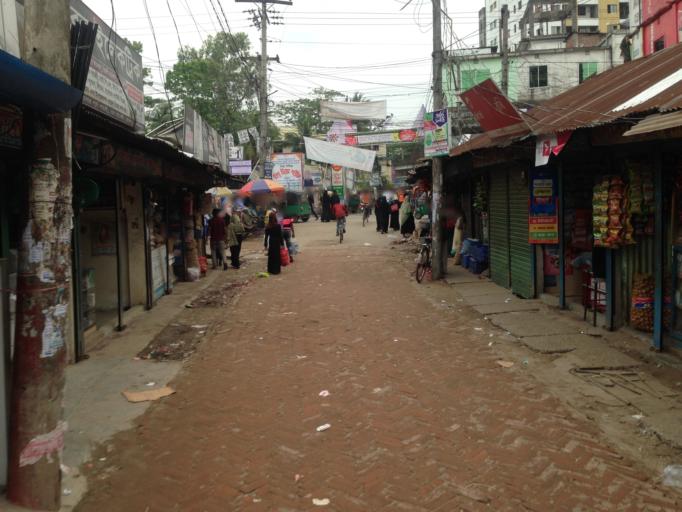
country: BD
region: Chittagong
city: Raipur
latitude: 23.0366
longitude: 90.7686
